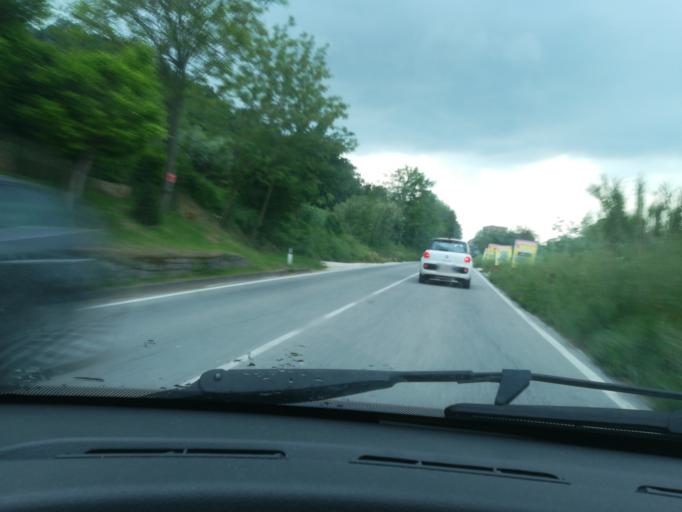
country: IT
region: The Marches
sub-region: Provincia di Macerata
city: Passo di Treia
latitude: 43.2832
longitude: 13.3385
